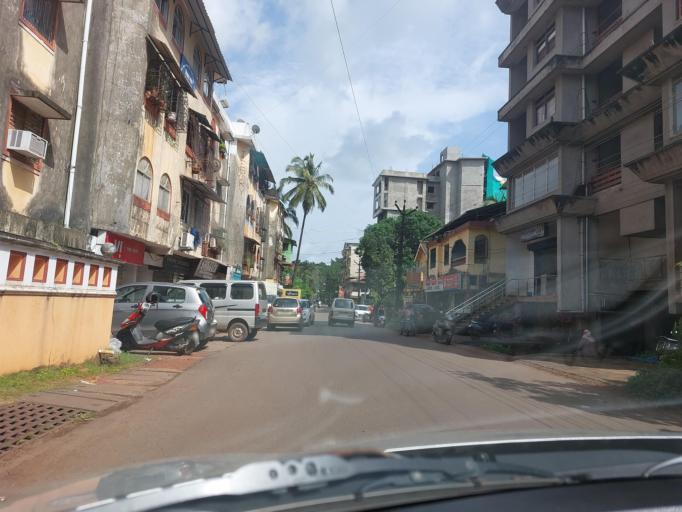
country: IN
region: Goa
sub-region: North Goa
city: Ponda
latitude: 15.3990
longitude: 74.0066
